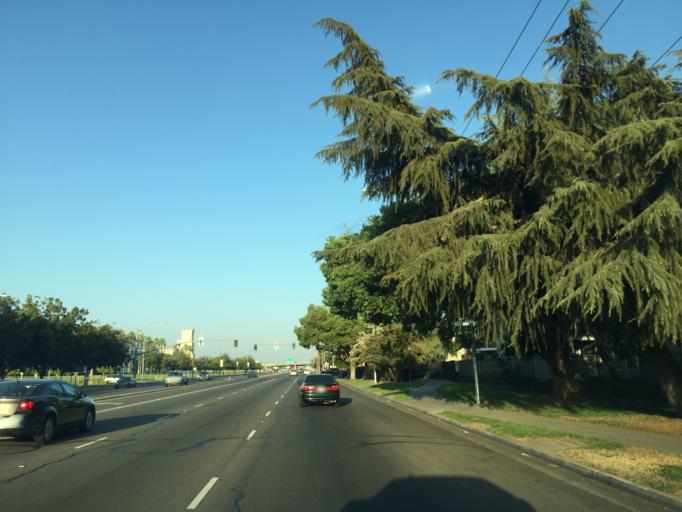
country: US
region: California
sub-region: Fresno County
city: Clovis
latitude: 36.8085
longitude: -119.7422
